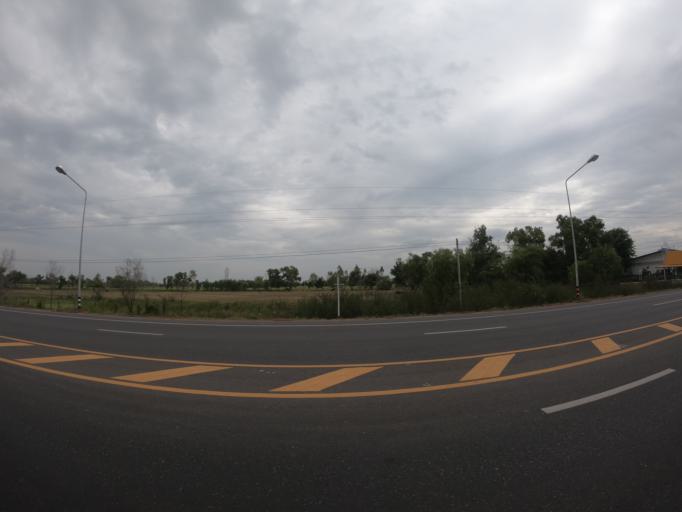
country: TH
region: Roi Et
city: Thawat Buri
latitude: 16.0875
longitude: 103.7591
